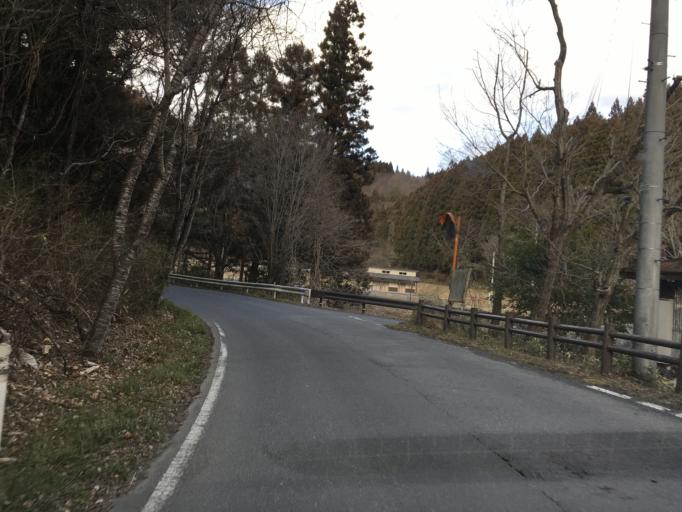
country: JP
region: Miyagi
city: Wakuya
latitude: 38.7168
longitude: 141.3079
